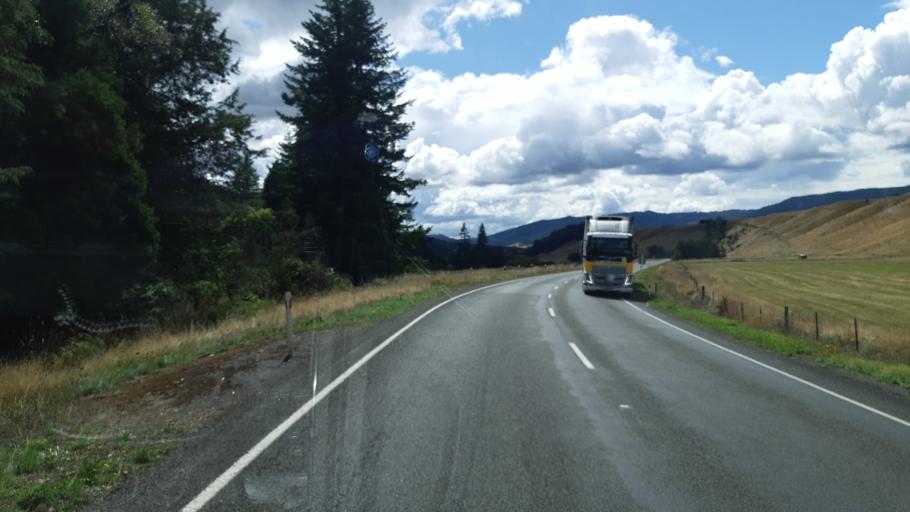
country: NZ
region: Tasman
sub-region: Tasman District
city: Wakefield
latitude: -41.5763
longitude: 172.7701
